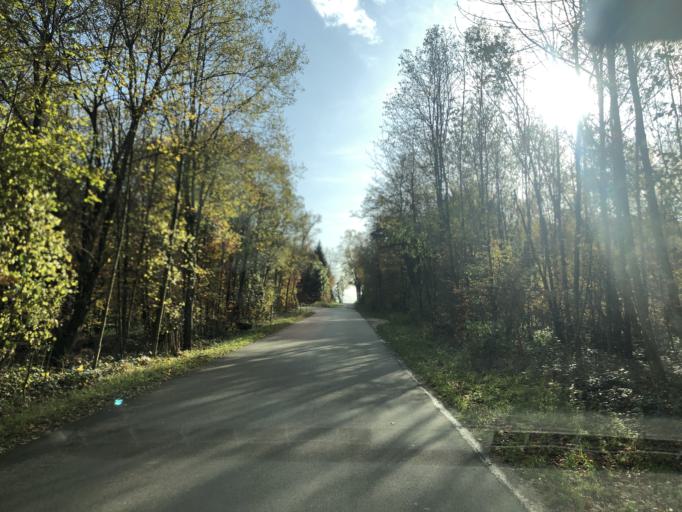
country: CH
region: Aargau
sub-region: Bezirk Baden
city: Obersiggenthal
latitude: 47.4725
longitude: 8.2786
